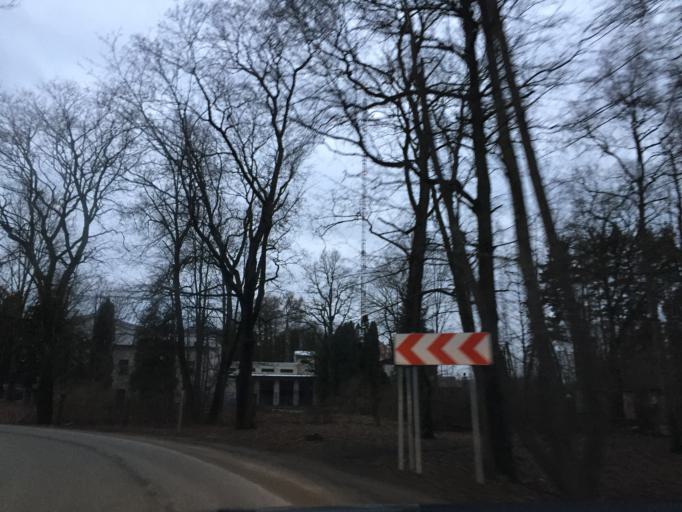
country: LV
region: Stopini
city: Ulbroka
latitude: 56.9406
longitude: 24.2858
